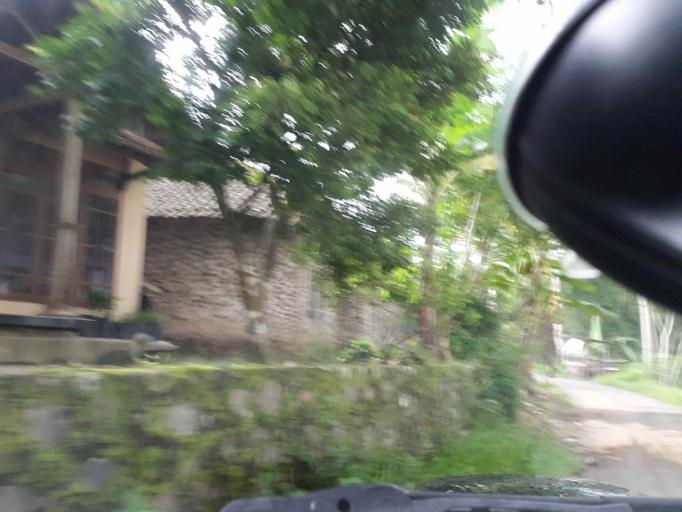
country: ID
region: Central Java
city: Wonosobo
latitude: -7.4800
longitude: 110.0040
